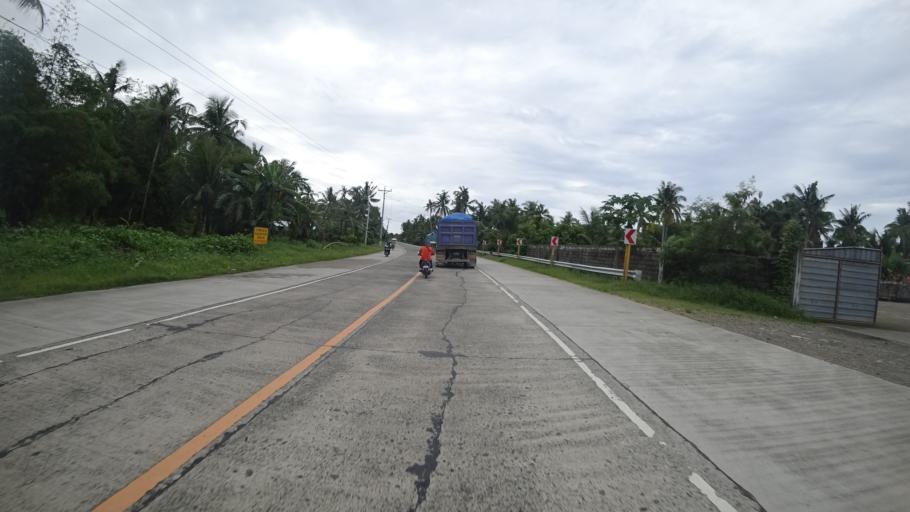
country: PH
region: Eastern Visayas
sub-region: Province of Leyte
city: MacArthur
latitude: 10.8514
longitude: 124.9955
